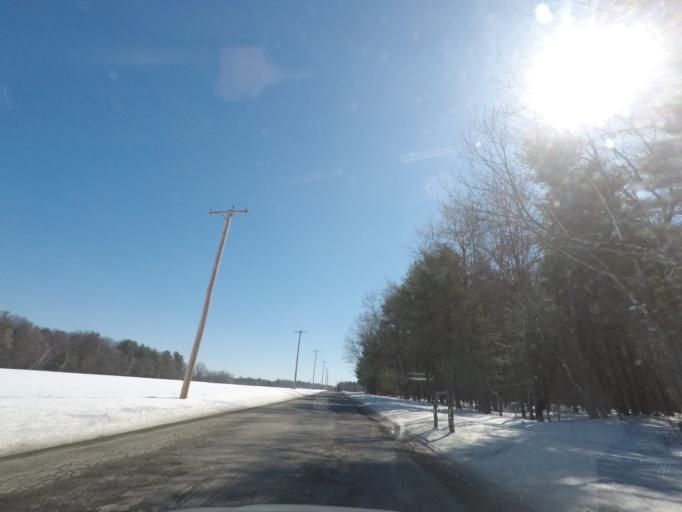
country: US
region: New York
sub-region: Saratoga County
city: Stillwater
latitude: 42.9171
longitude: -73.6161
